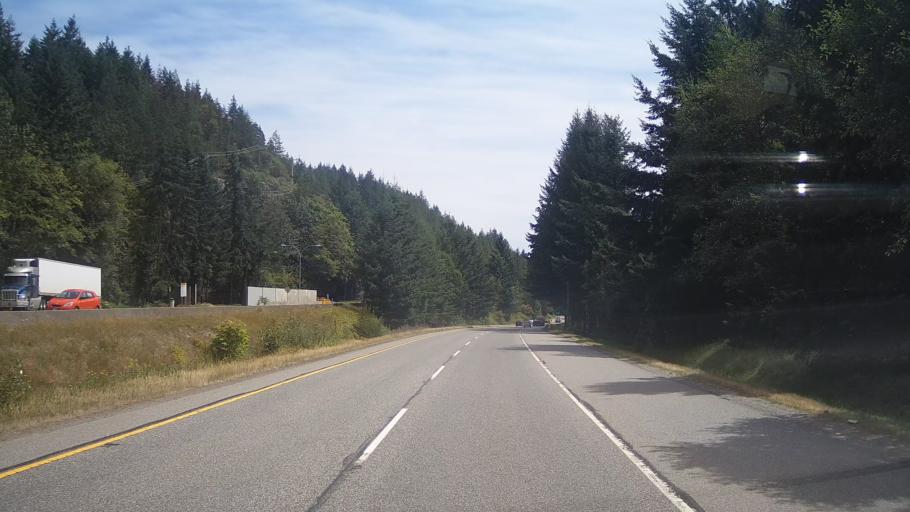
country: CA
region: British Columbia
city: West Vancouver
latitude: 49.3488
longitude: -123.2319
